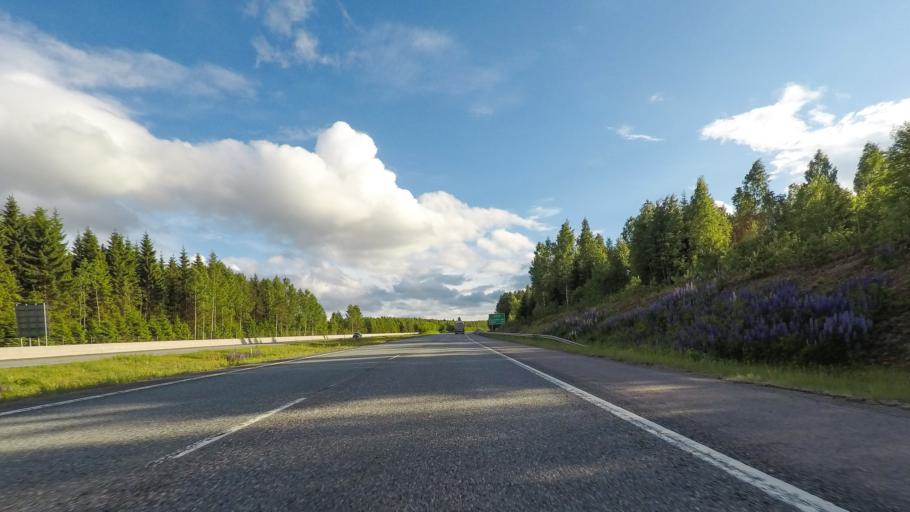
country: FI
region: Paijanne Tavastia
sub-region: Lahti
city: Heinola
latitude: 61.1504
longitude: 25.9723
